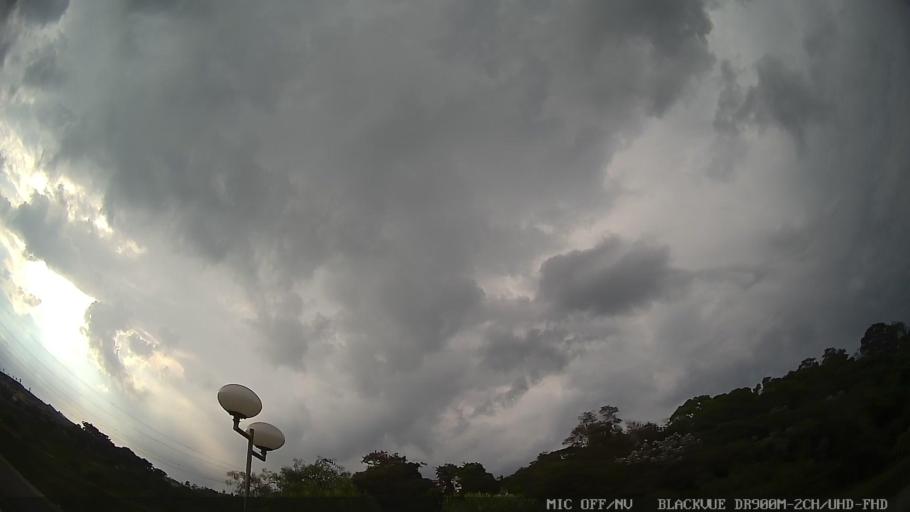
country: BR
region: Sao Paulo
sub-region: Itatiba
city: Itatiba
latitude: -23.0277
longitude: -46.8477
